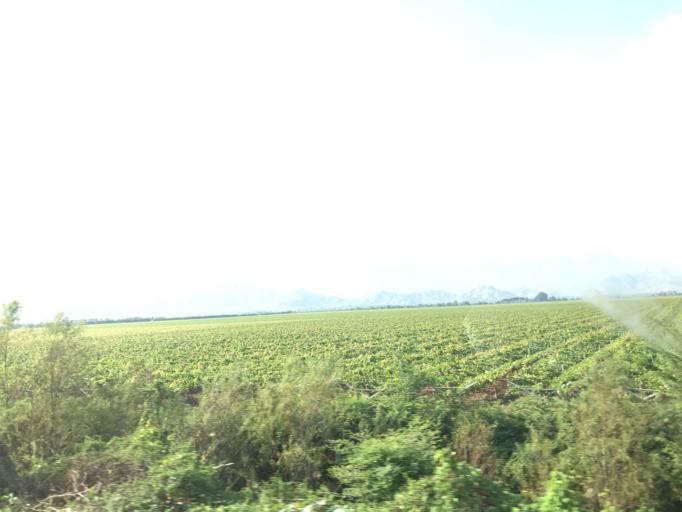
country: PE
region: Lambayeque
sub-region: Provincia de Chiclayo
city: Chongoyape
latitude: -6.6584
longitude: -79.4311
